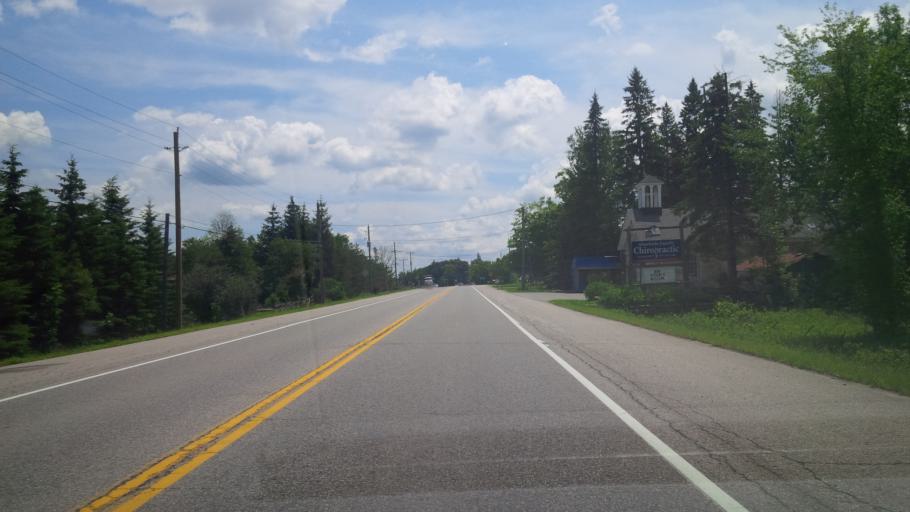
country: CA
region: Ontario
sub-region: Wellington County
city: Guelph
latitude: 43.4773
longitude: -80.1580
